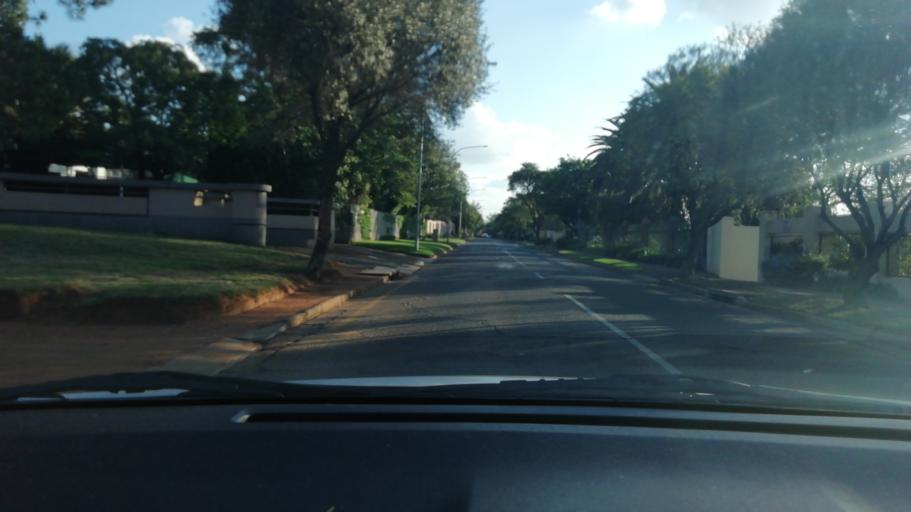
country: ZA
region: Gauteng
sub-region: Ekurhuleni Metropolitan Municipality
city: Benoni
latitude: -26.1954
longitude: 28.2993
